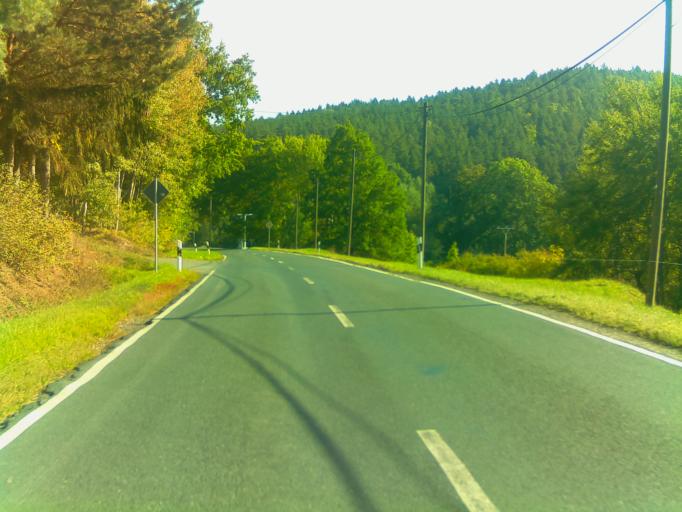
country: DE
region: Thuringia
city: Saara
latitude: 50.8354
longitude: 11.9551
